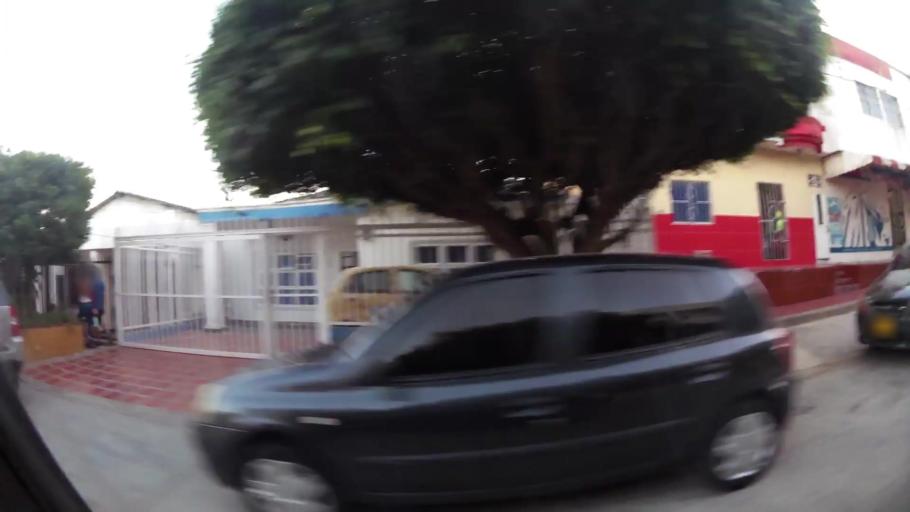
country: CO
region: Atlantico
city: Barranquilla
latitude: 10.9794
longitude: -74.8117
